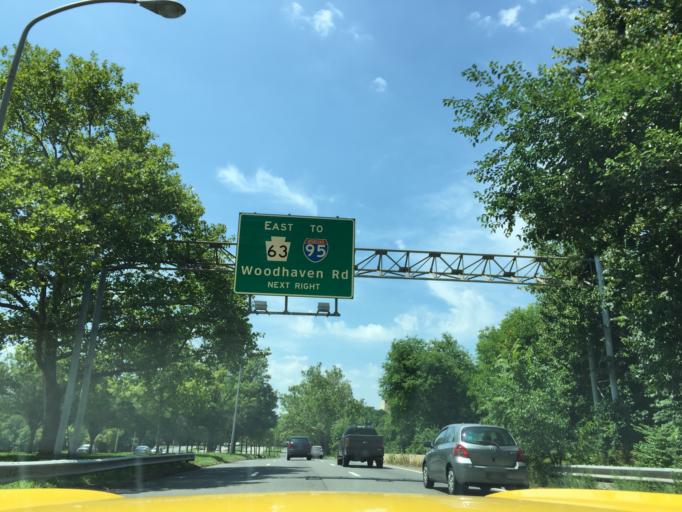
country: US
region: Pennsylvania
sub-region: Bucks County
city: Trevose
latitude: 40.1106
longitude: -74.9935
